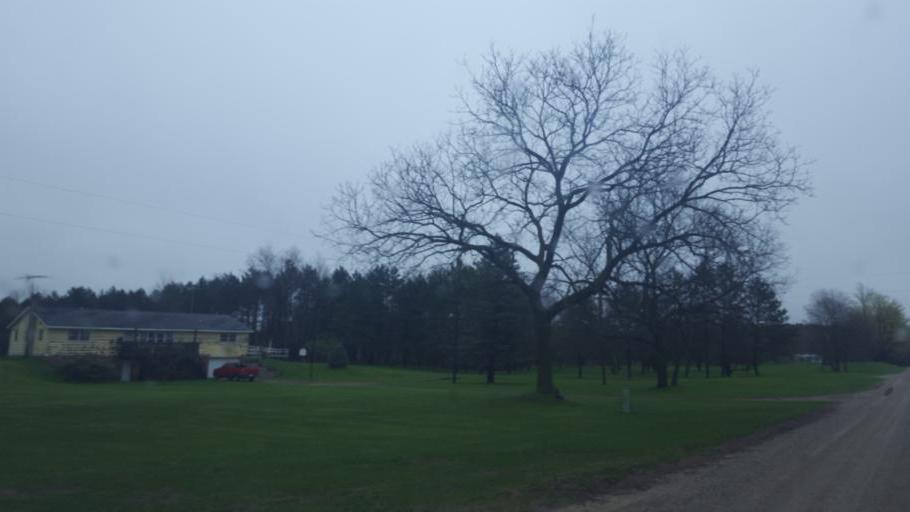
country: US
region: Michigan
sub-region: Isabella County
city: Lake Isabella
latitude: 43.5672
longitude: -85.0161
